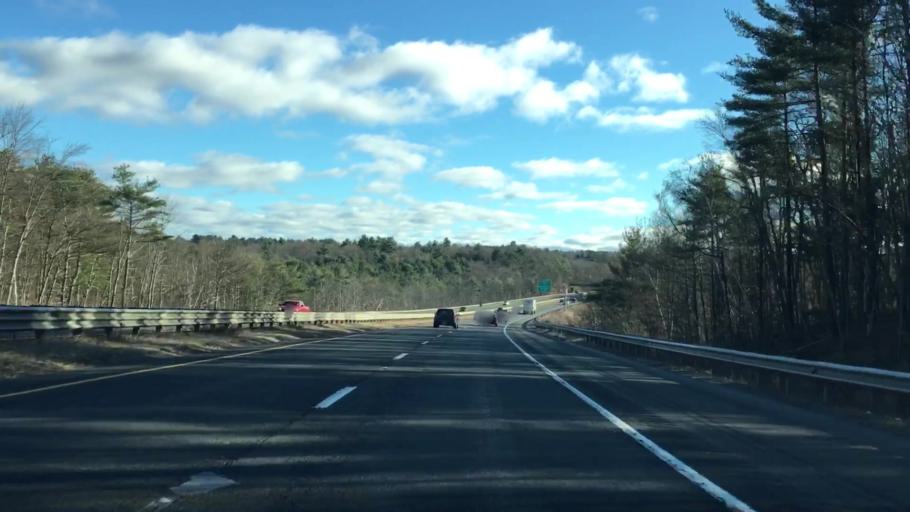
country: US
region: Massachusetts
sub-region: Worcester County
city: Sturbridge
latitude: 42.1360
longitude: -72.0886
